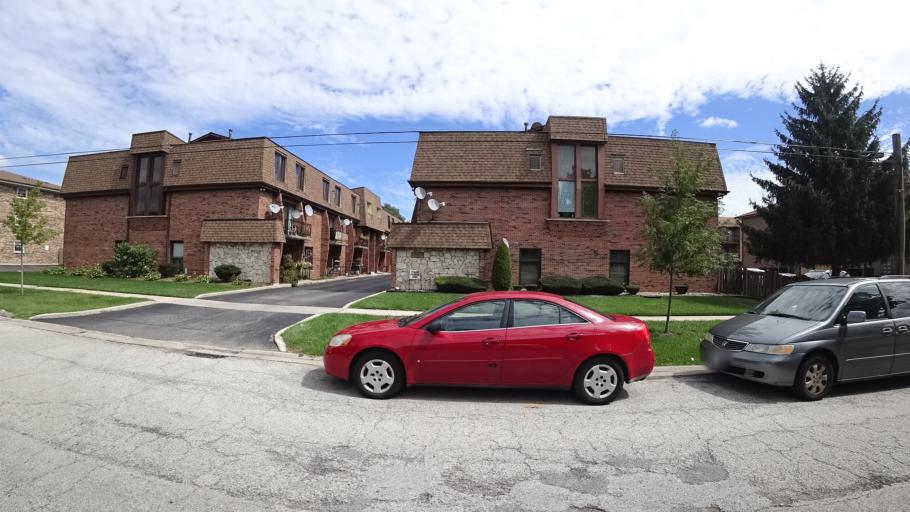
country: US
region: Illinois
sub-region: Cook County
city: Chicago Ridge
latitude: 41.7126
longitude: -87.7961
